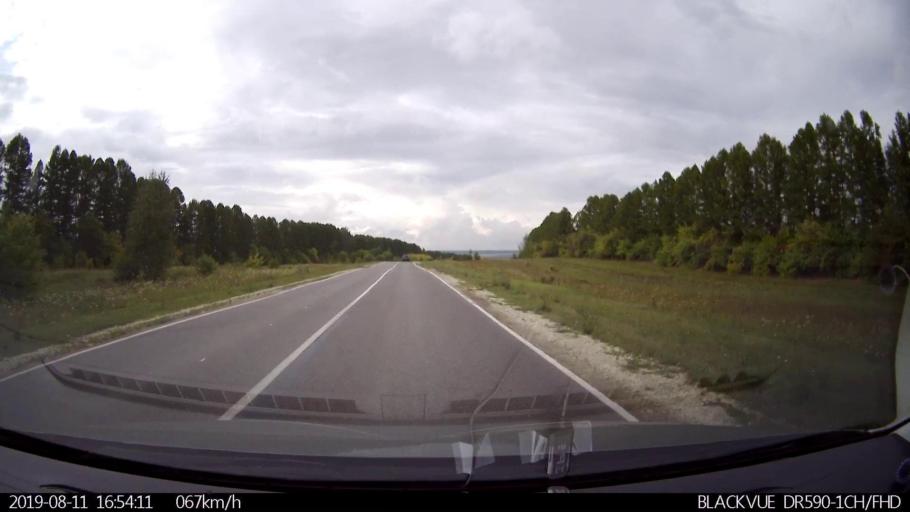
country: RU
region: Ulyanovsk
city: Mayna
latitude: 54.2701
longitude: 47.6669
